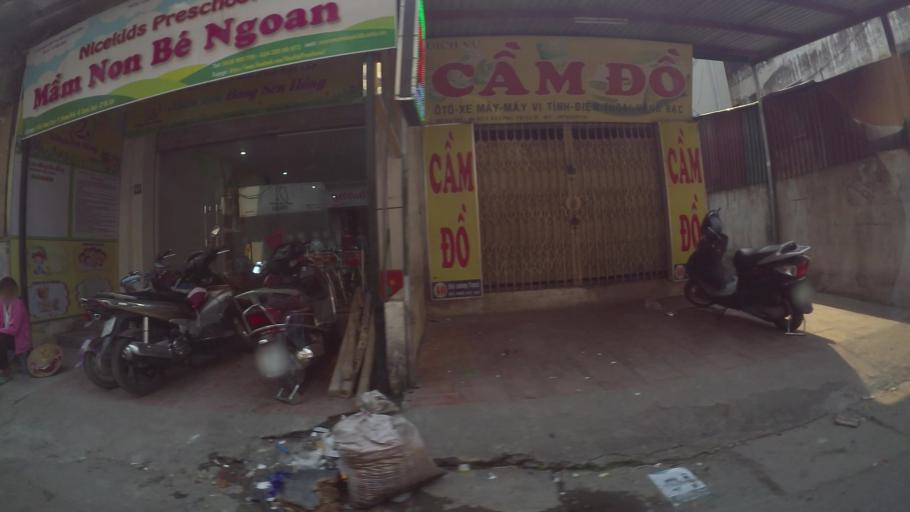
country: VN
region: Ha Noi
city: Thanh Xuan
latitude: 20.9911
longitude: 105.8173
